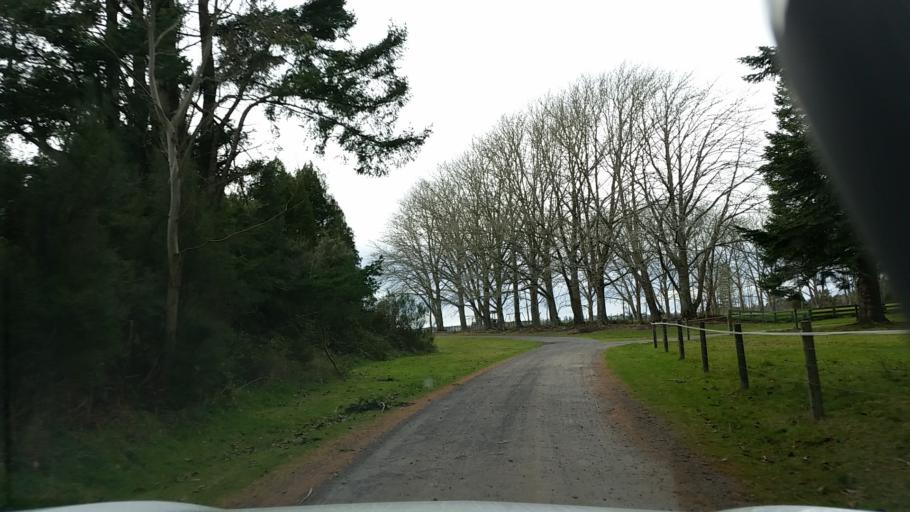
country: NZ
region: Bay of Plenty
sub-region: Whakatane District
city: Murupara
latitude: -38.3071
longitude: 176.4999
